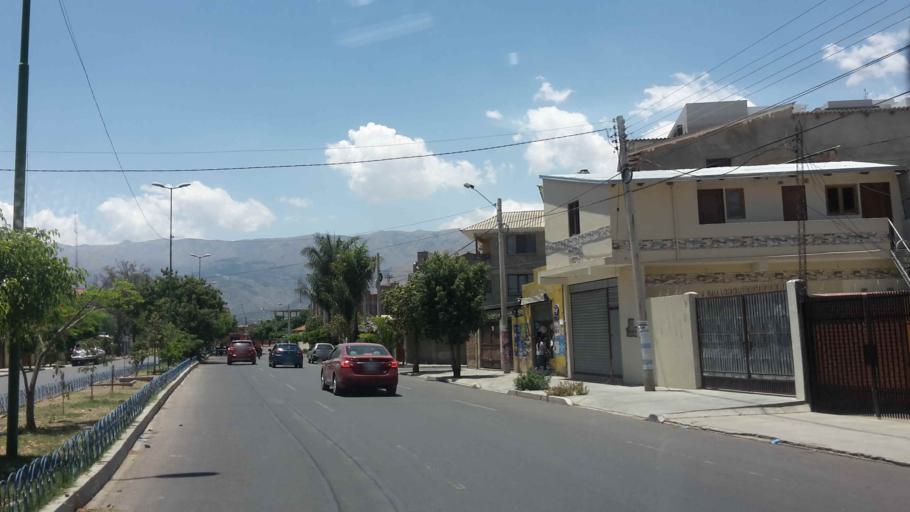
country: BO
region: Cochabamba
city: Cochabamba
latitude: -17.3843
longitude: -66.1883
